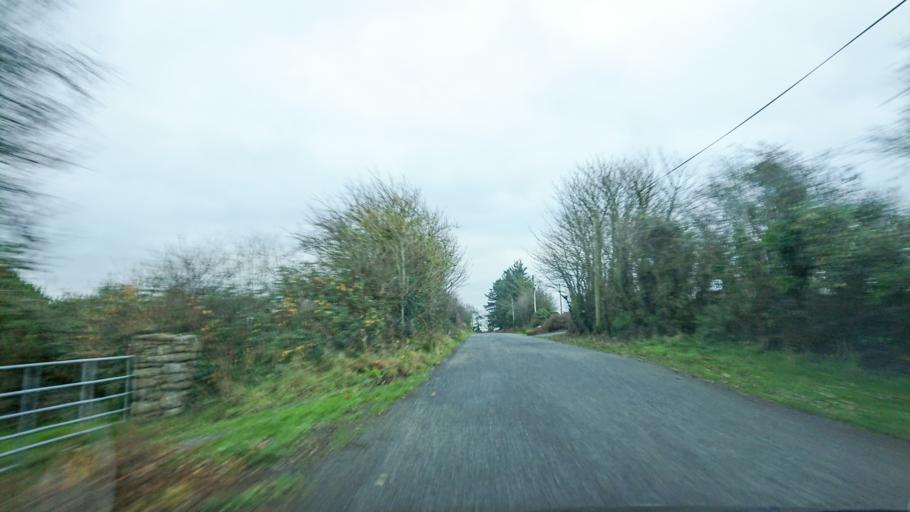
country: IE
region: Munster
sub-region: Waterford
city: Dunmore East
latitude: 52.2387
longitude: -6.9900
